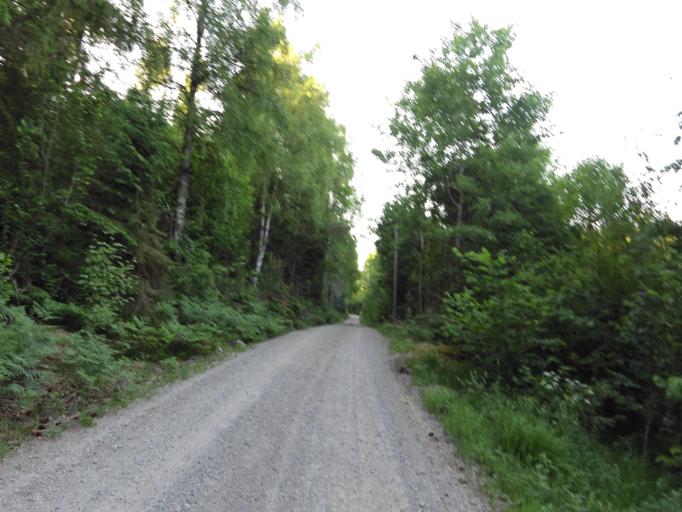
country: SE
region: Blekinge
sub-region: Olofstroms Kommun
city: Olofstroem
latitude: 56.4086
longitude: 14.5604
